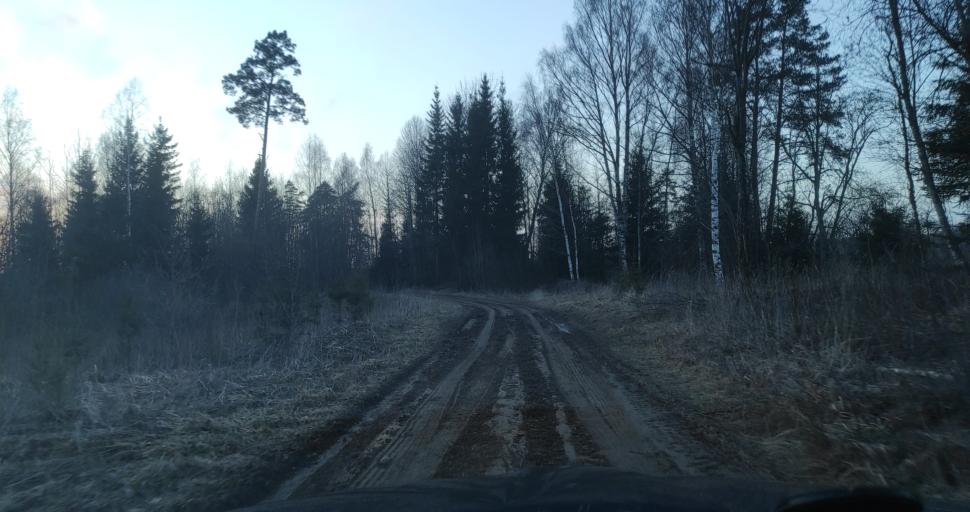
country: LV
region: Kuldigas Rajons
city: Kuldiga
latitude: 56.8128
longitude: 21.8241
